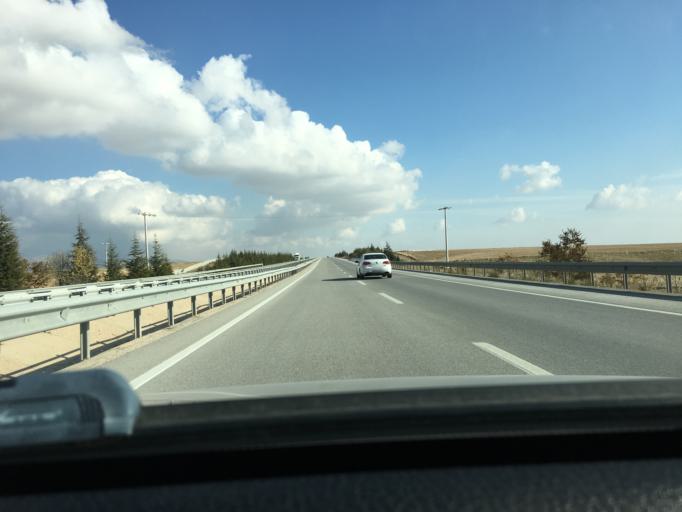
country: TR
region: Eskisehir
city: Kaymaz
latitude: 39.4842
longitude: 31.2886
